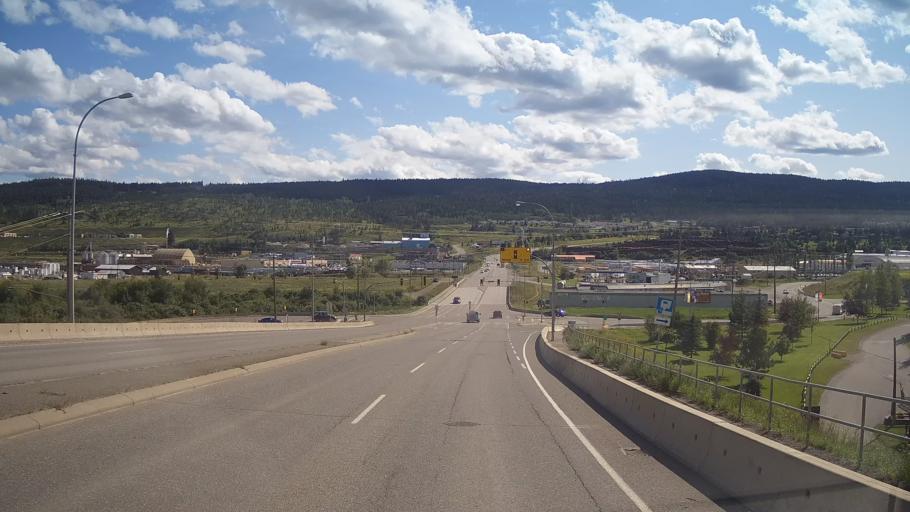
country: CA
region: British Columbia
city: Williams Lake
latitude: 52.1248
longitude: -122.1287
